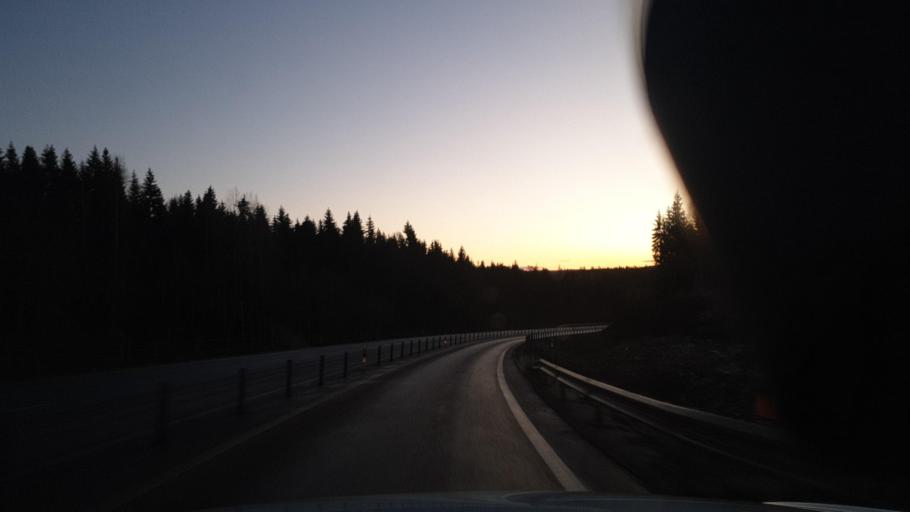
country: SE
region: Vaermland
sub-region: Eda Kommun
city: Amotfors
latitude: 59.7581
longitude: 12.4686
